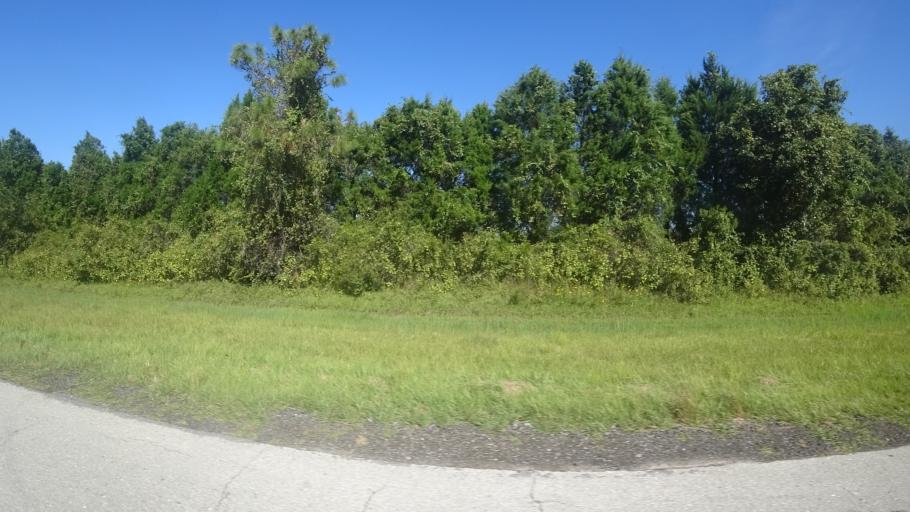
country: US
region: Florida
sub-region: Sarasota County
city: Warm Mineral Springs
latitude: 27.2737
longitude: -82.1359
